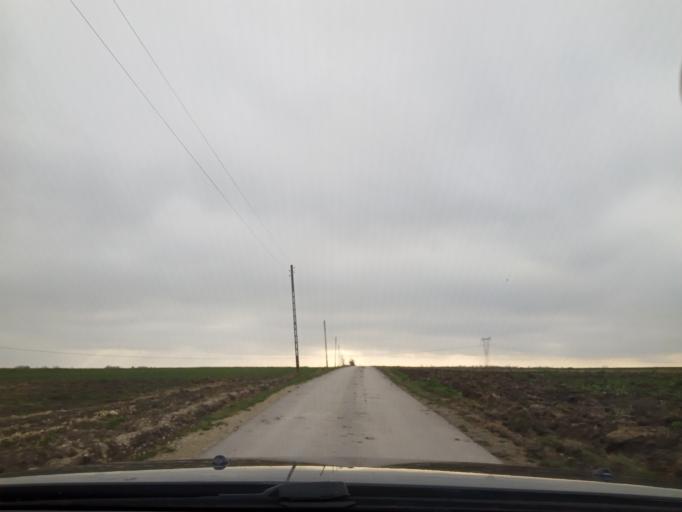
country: PL
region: Swietokrzyskie
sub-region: Powiat jedrzejowski
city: Imielno
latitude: 50.6183
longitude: 20.3945
